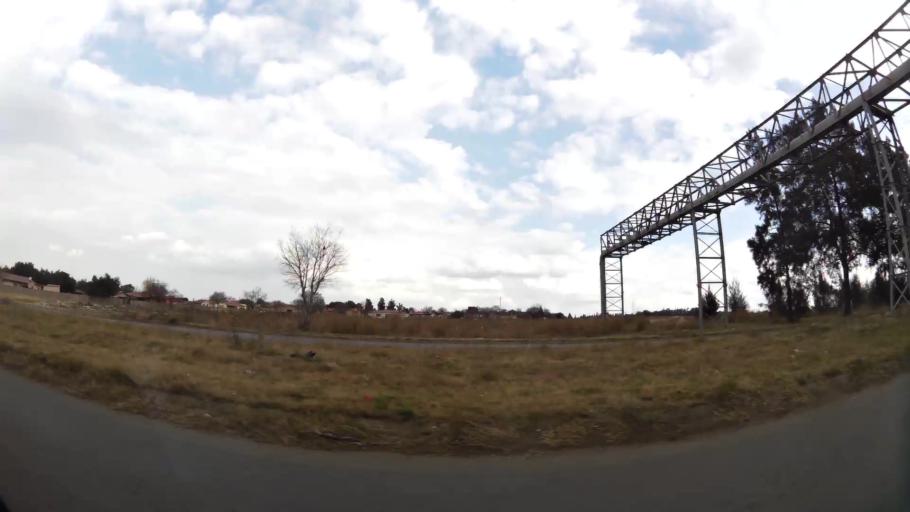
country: ZA
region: Gauteng
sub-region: Sedibeng District Municipality
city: Vanderbijlpark
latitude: -26.6739
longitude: 27.8312
